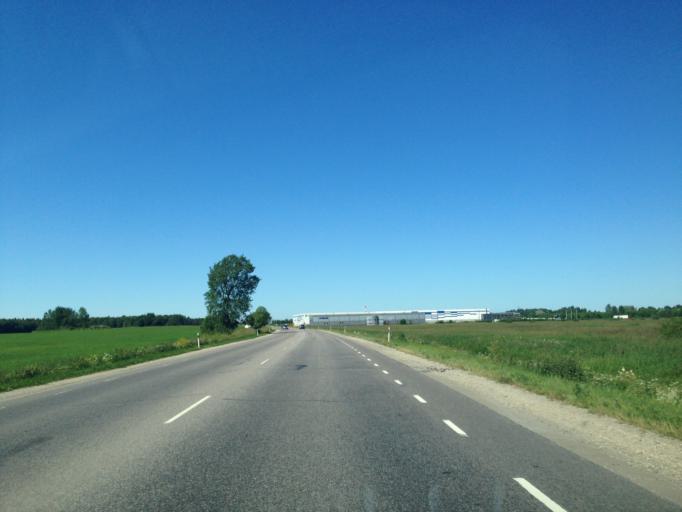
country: EE
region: Harju
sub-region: Rae vald
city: Jueri
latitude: 59.3879
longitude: 24.9199
